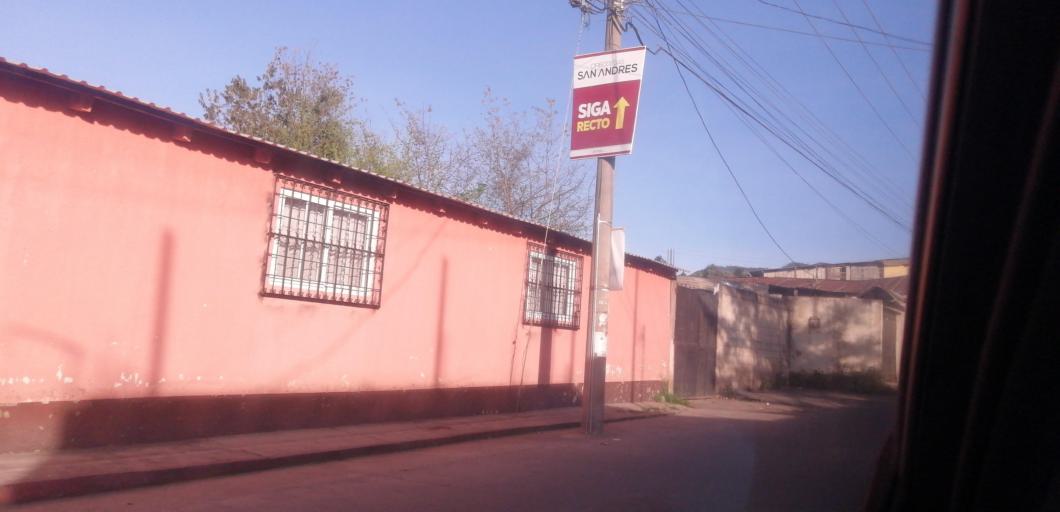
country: GT
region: Quetzaltenango
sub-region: Municipio de La Esperanza
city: La Esperanza
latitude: 14.8645
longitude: -91.5385
